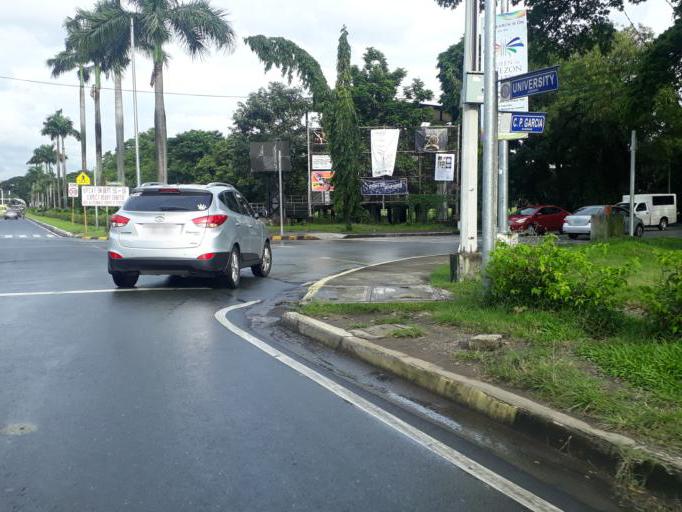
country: PH
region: Metro Manila
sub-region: Quezon City
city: Quezon City
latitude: 14.6547
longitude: 121.0581
